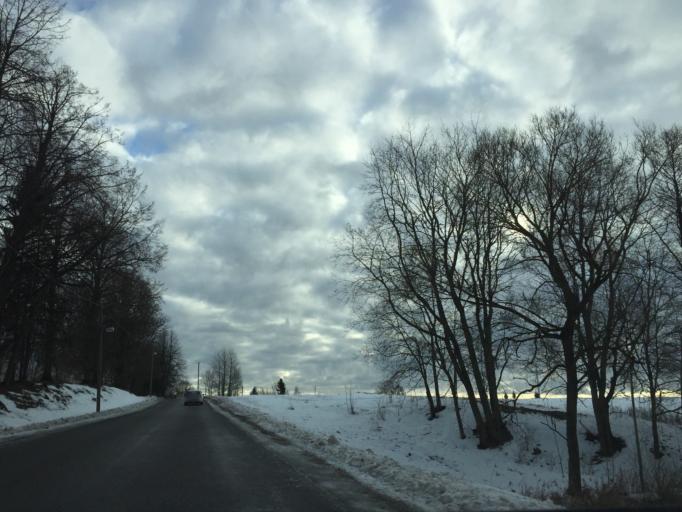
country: LV
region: Lielvarde
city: Lielvarde
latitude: 56.6303
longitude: 24.7580
